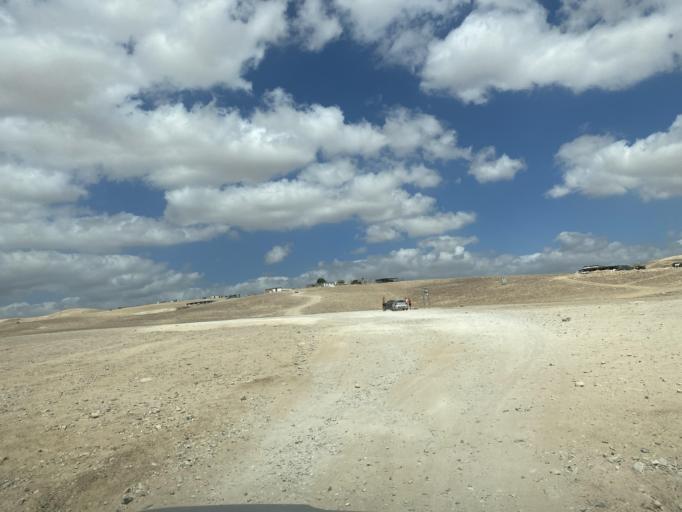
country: PS
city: `Arab ar Rashaydah
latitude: 31.5325
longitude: 35.2842
